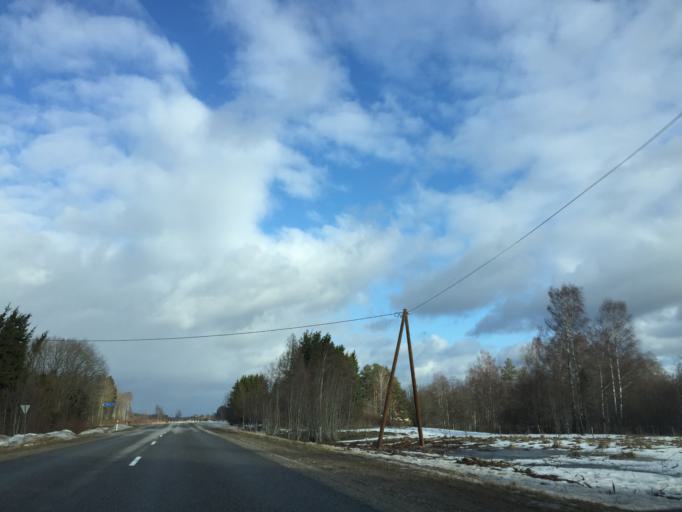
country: LV
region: Aloja
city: Staicele
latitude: 57.8712
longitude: 24.5722
